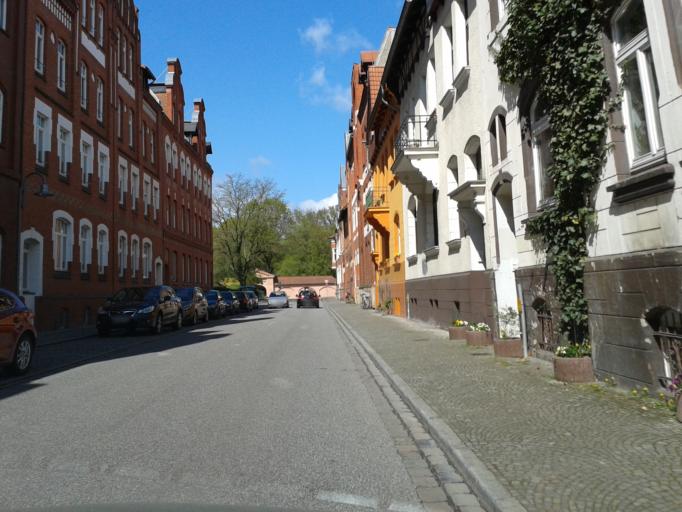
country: DE
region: Saxony-Anhalt
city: Salzwedel
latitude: 52.8534
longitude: 11.1516
